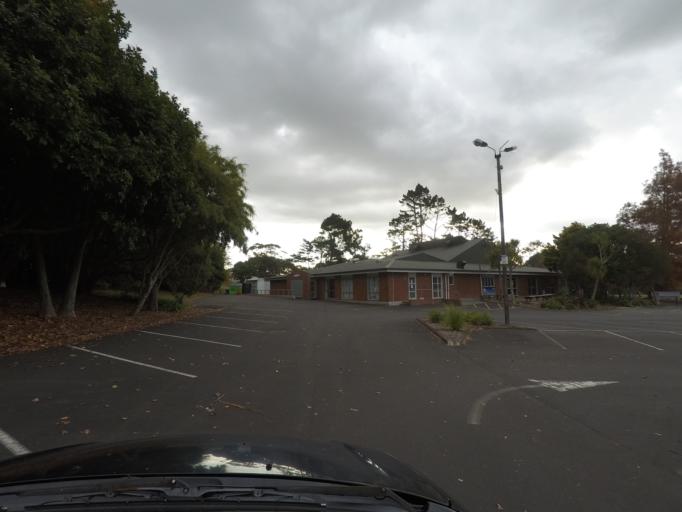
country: NZ
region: Auckland
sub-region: Auckland
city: Rosebank
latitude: -36.8288
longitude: 174.6297
